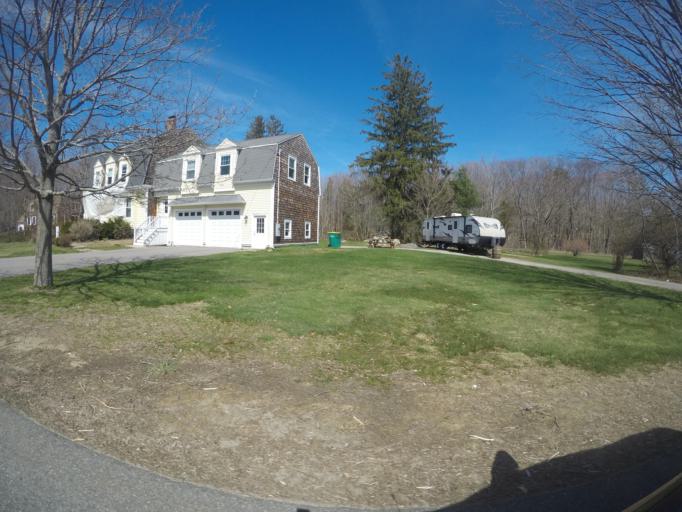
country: US
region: Massachusetts
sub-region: Bristol County
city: Easton
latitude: 42.0279
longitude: -71.0843
